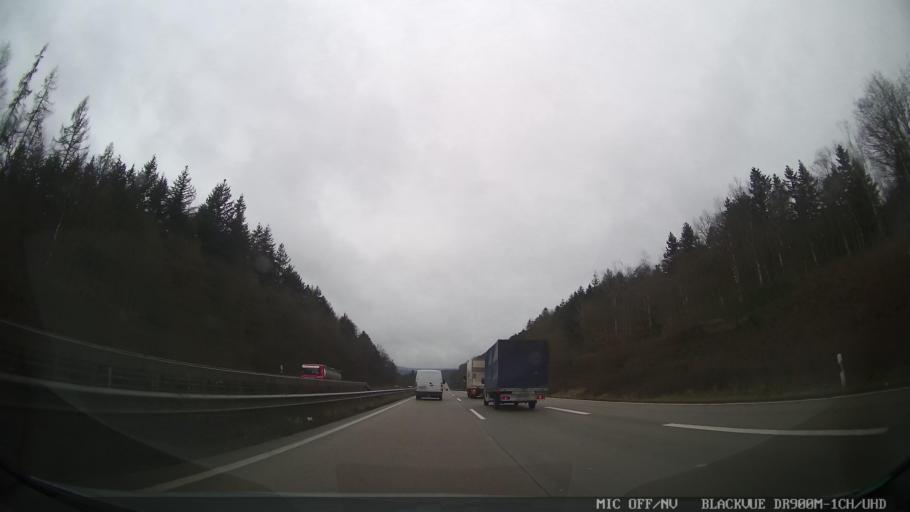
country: DE
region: Rheinland-Pfalz
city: Mehlingen
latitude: 49.4591
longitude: 7.8518
